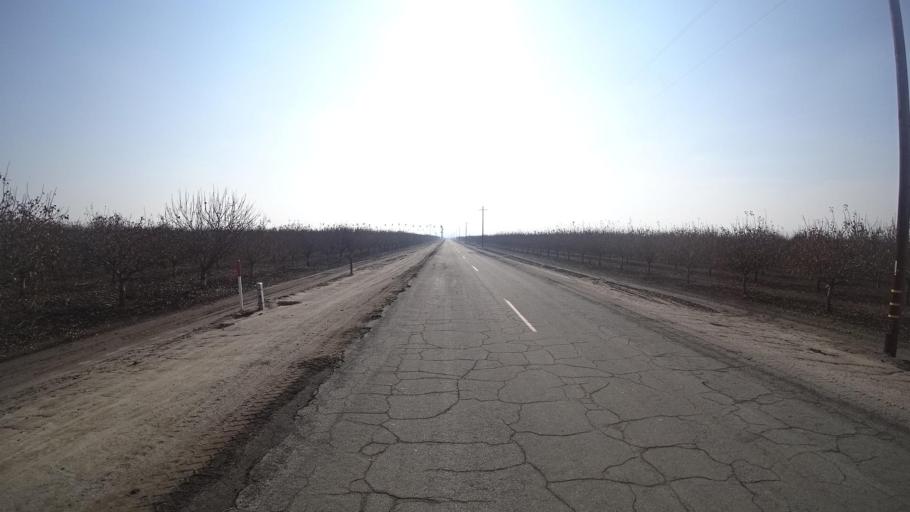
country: US
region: California
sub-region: Kern County
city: Buttonwillow
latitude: 35.3458
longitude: -119.3945
